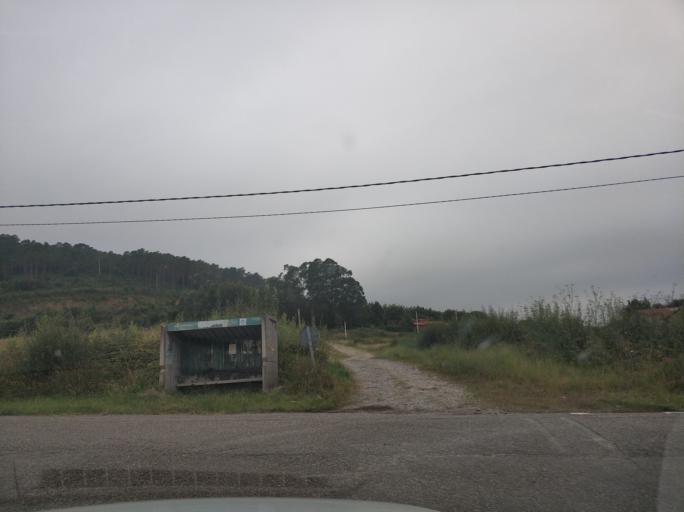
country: ES
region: Asturias
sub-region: Province of Asturias
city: Cudillero
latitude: 43.5609
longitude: -6.1777
